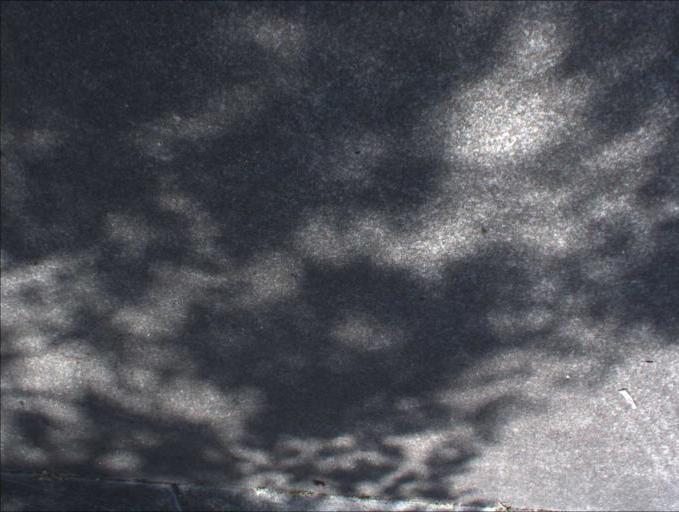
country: AU
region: Queensland
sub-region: Logan
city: Rochedale South
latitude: -27.5949
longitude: 153.1318
